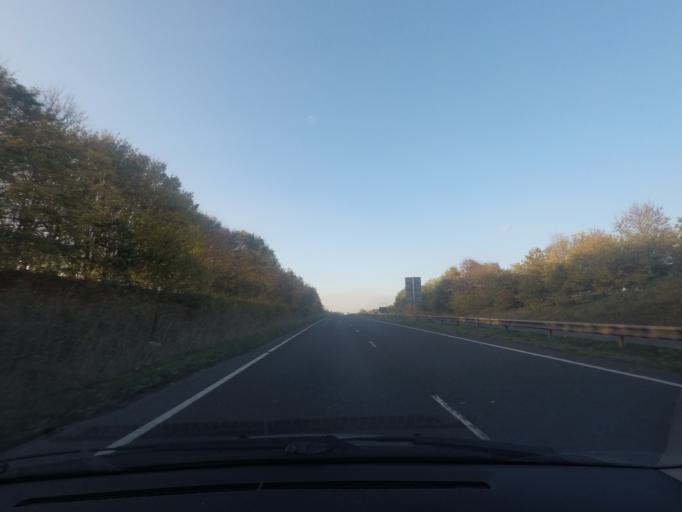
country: GB
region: England
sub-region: North Lincolnshire
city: Barnetby le Wold
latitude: 53.5931
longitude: -0.4180
